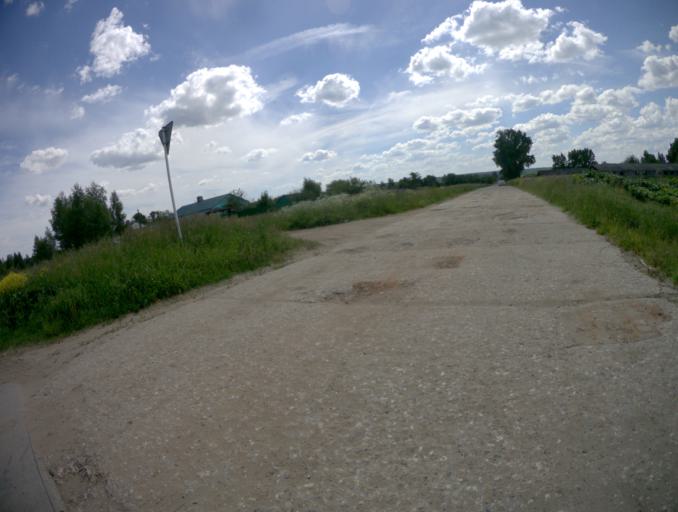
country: RU
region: Ivanovo
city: Gavrilov Posad
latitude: 56.3794
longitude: 40.0265
